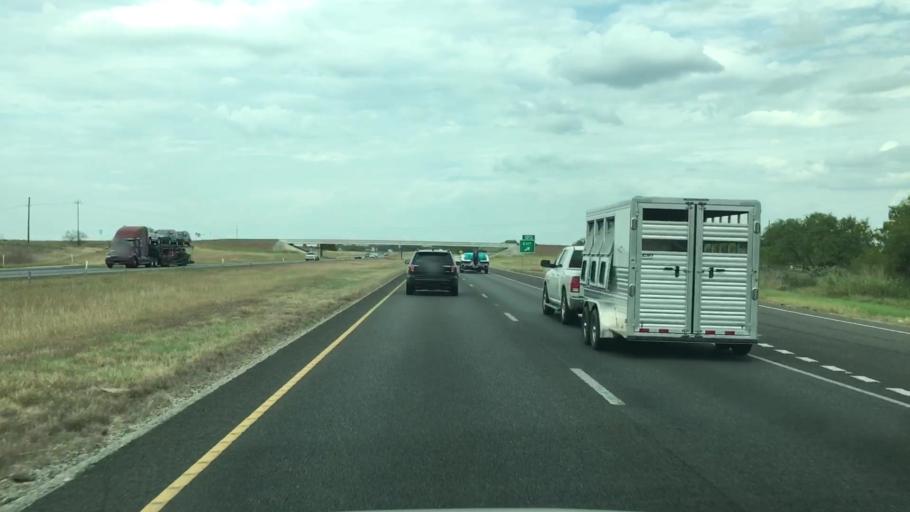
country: US
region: Texas
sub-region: Bexar County
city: Elmendorf
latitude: 29.1388
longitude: -98.4290
